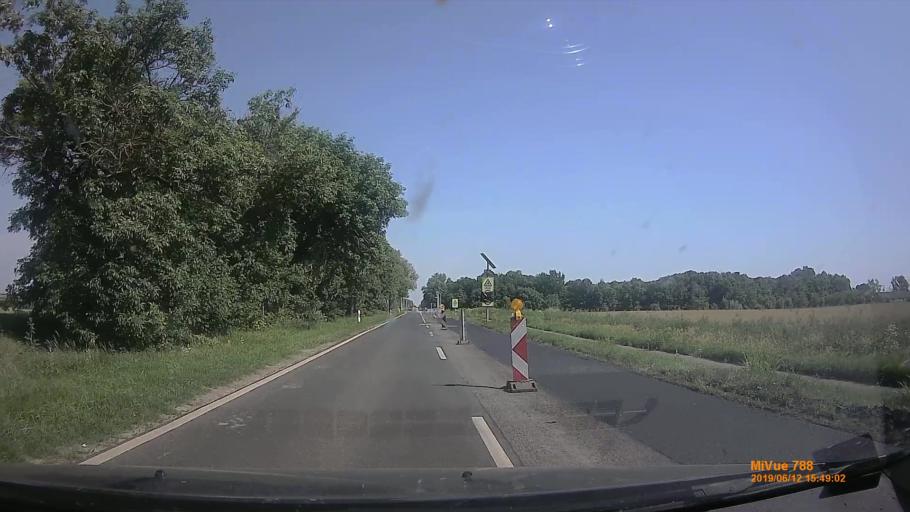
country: HU
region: Csongrad
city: Apatfalva
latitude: 46.1983
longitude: 20.5554
